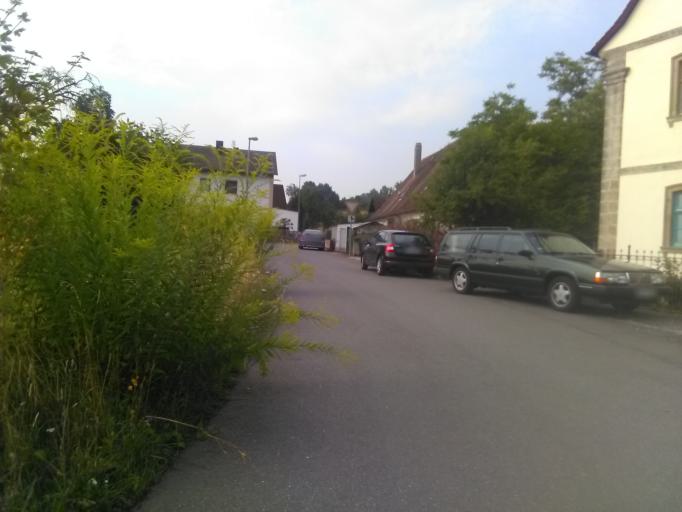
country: DE
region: Bavaria
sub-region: Upper Franconia
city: Pettstadt
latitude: 49.8394
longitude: 10.9268
